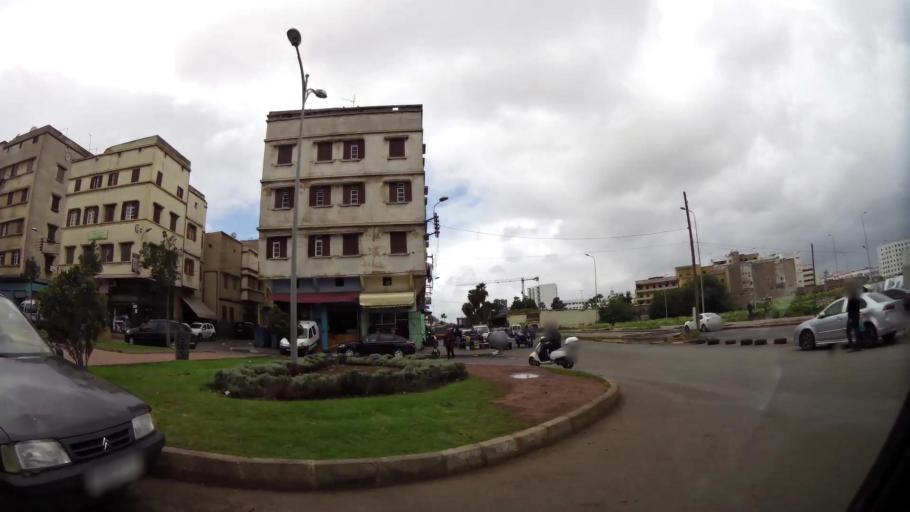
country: MA
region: Grand Casablanca
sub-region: Casablanca
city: Casablanca
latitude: 33.5656
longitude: -7.5929
